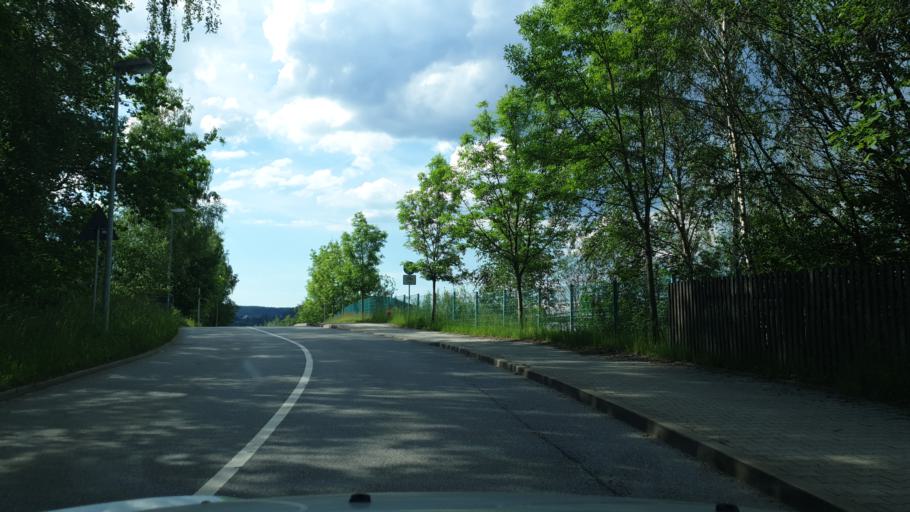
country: DE
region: Saxony
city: Schwarzenberg
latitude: 50.5469
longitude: 12.7701
